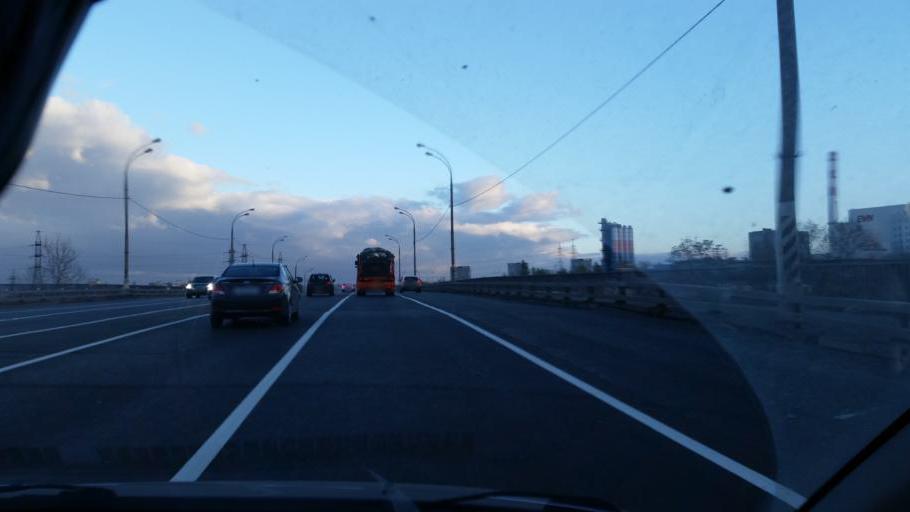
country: RU
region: Moskovskaya
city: Biryulevo Zapadnoye
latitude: 55.6047
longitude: 37.6319
